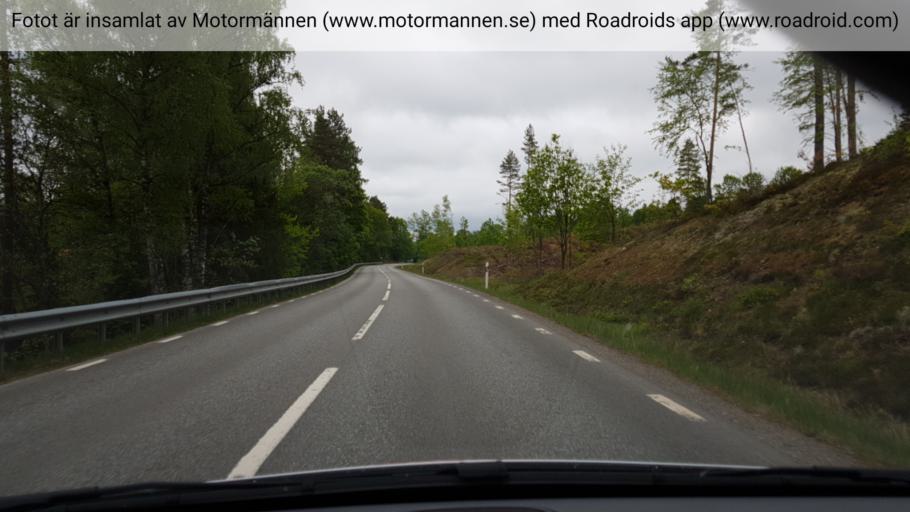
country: SE
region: Joenkoeping
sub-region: Mullsjo Kommun
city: Mullsjoe
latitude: 57.8174
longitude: 13.8523
